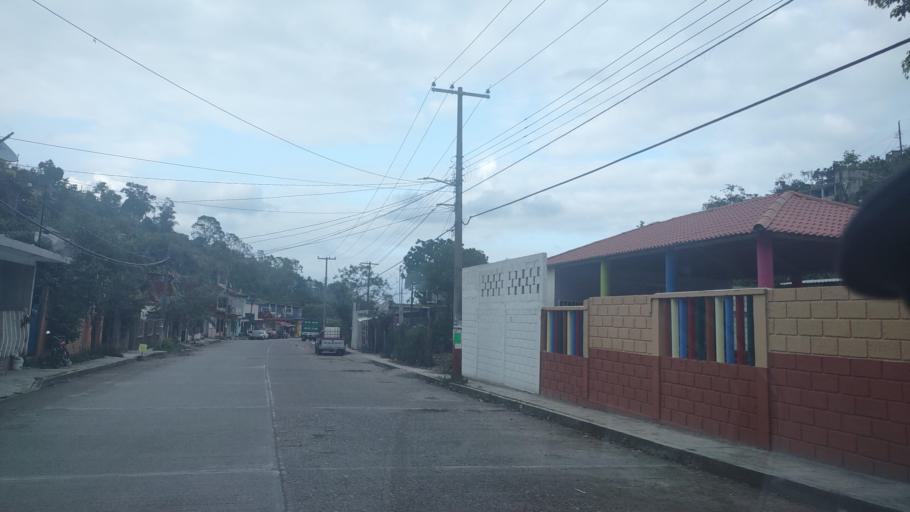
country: MX
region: Veracruz
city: Papantla de Olarte
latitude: 20.4502
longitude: -97.3130
